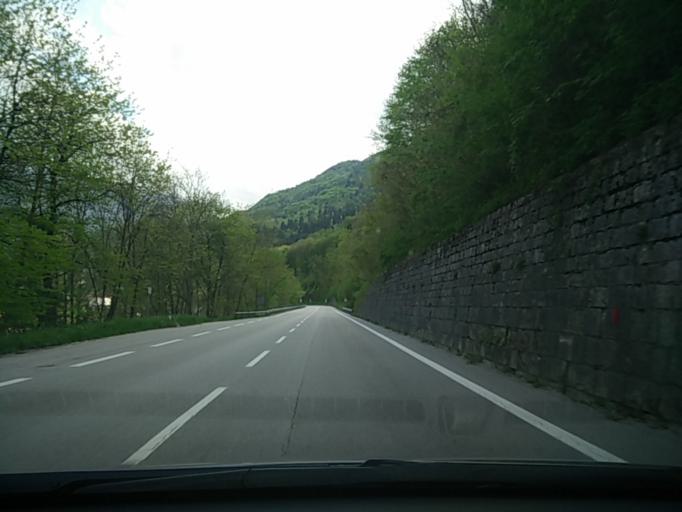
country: IT
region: Veneto
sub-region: Provincia di Belluno
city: Farra d'Alpago
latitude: 46.0990
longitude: 12.3259
